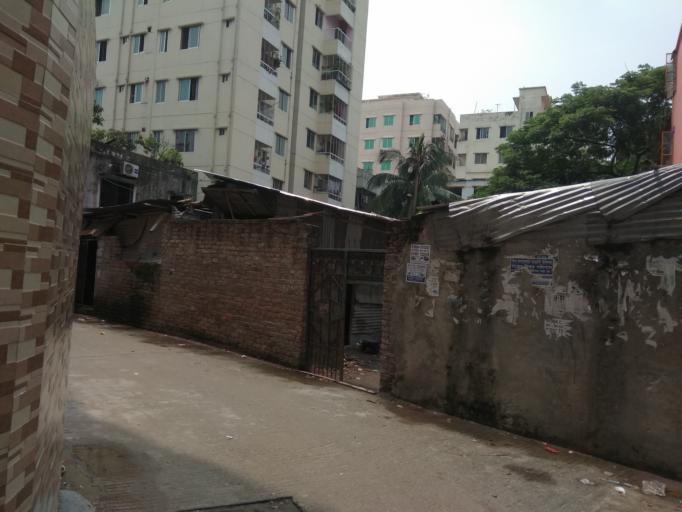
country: BD
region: Dhaka
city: Azimpur
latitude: 23.7981
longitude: 90.3746
